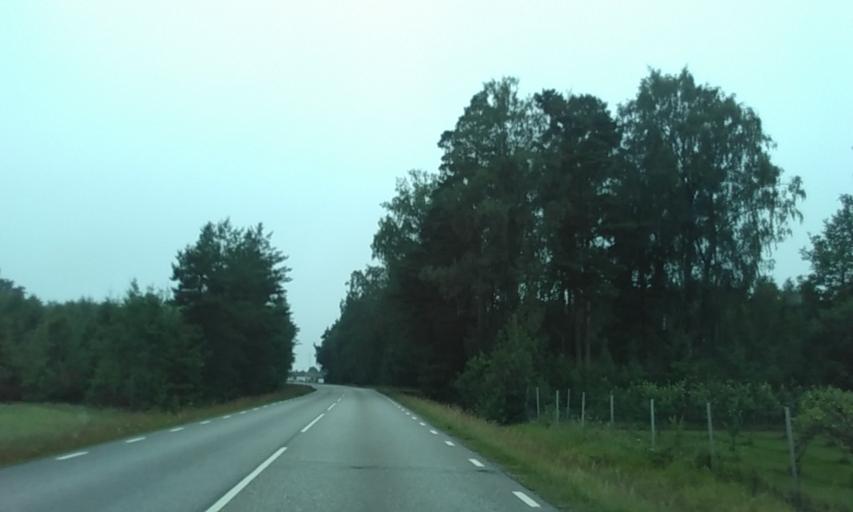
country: SE
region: Vaestra Goetaland
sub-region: Vargarda Kommun
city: Vargarda
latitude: 58.1560
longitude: 12.8361
